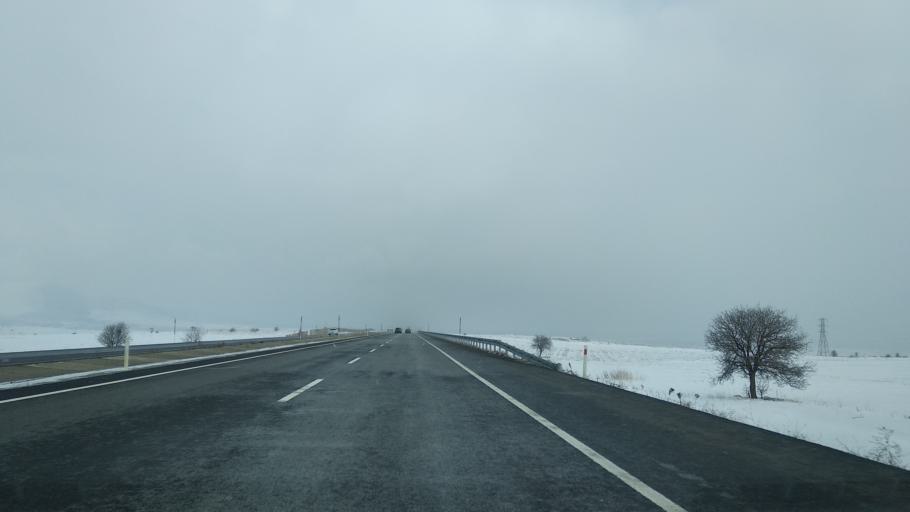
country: TR
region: Kayseri
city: Elbasi
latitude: 38.6286
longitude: 35.8292
